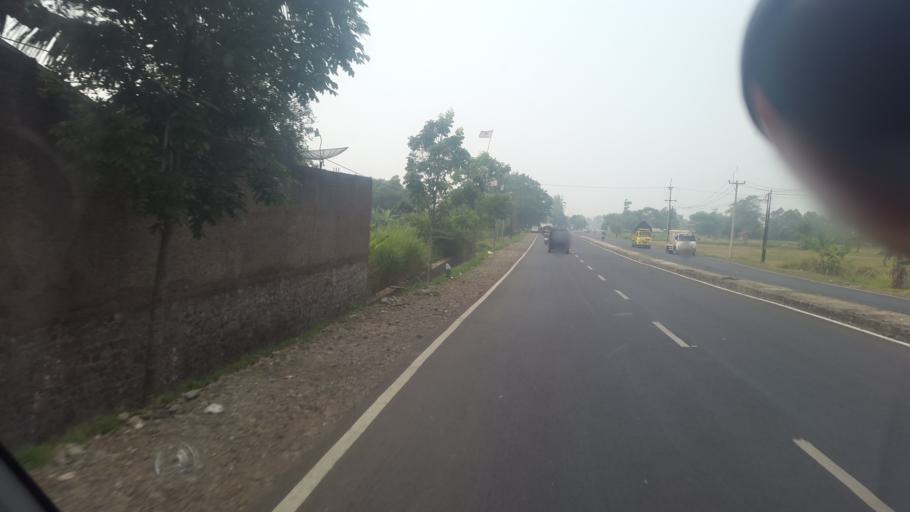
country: ID
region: West Java
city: Sukabumi
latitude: -6.9336
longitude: 106.9035
